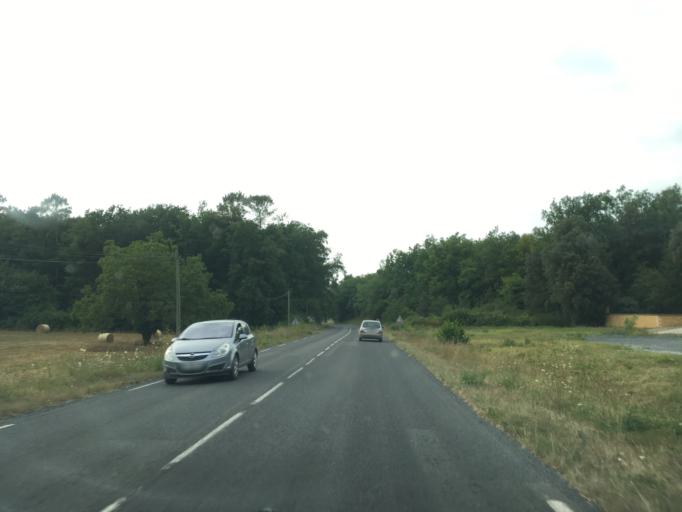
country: FR
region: Aquitaine
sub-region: Departement de la Dordogne
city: Carsac-Aillac
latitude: 44.8651
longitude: 1.2931
